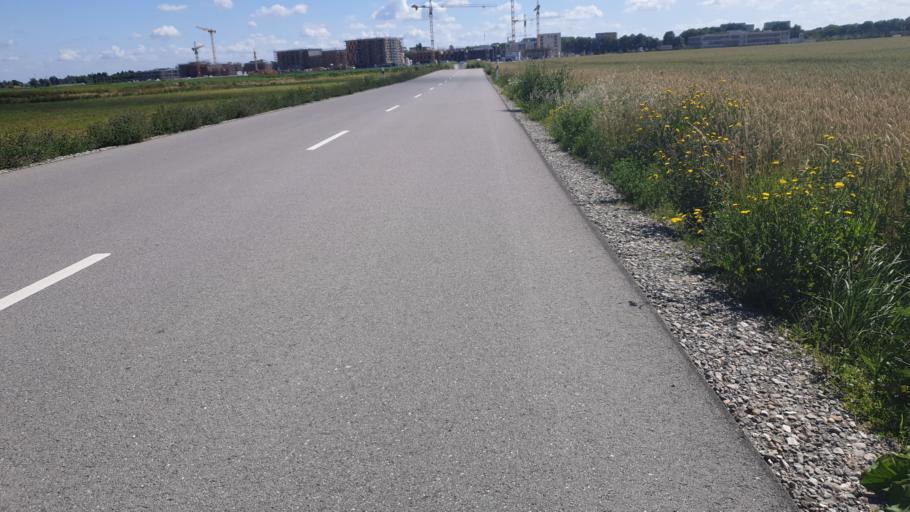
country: DE
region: Bavaria
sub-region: Upper Bavaria
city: Germering
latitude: 48.1457
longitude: 11.3988
